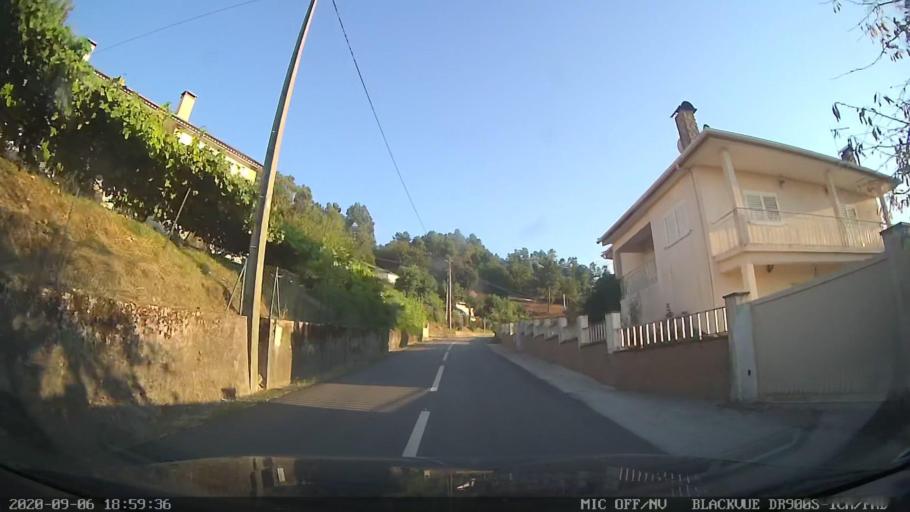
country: PT
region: Porto
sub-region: Baiao
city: Baiao
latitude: 41.2421
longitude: -7.9962
